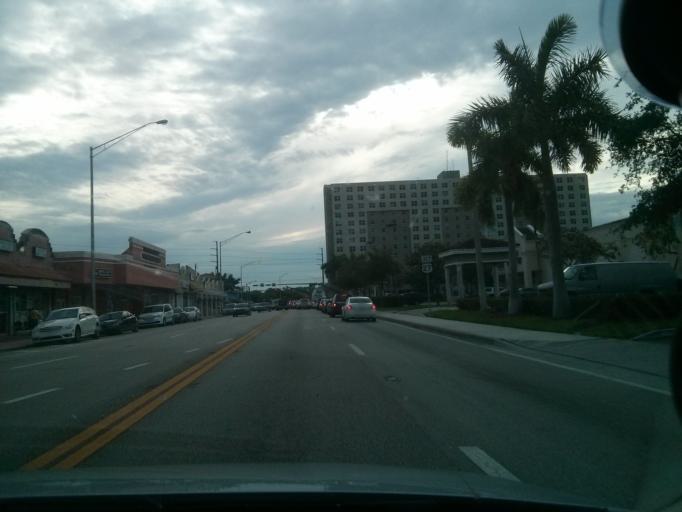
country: US
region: Florida
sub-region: Miami-Dade County
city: Miami Springs
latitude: 25.8228
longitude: -80.2776
